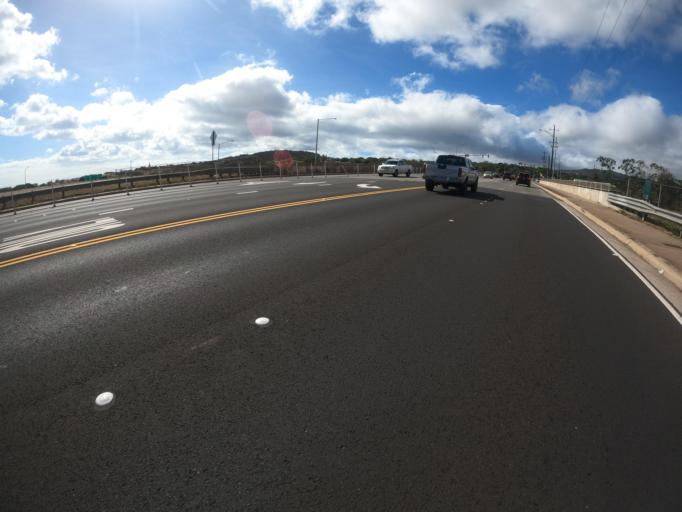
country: US
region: Hawaii
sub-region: Honolulu County
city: Makakilo City
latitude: 21.3418
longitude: -158.0774
